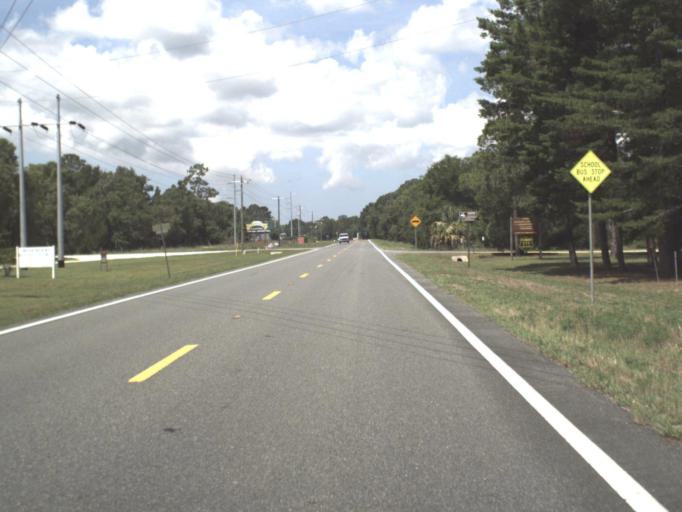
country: US
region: Florida
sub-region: Levy County
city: Chiefland
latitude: 29.2379
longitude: -82.9350
